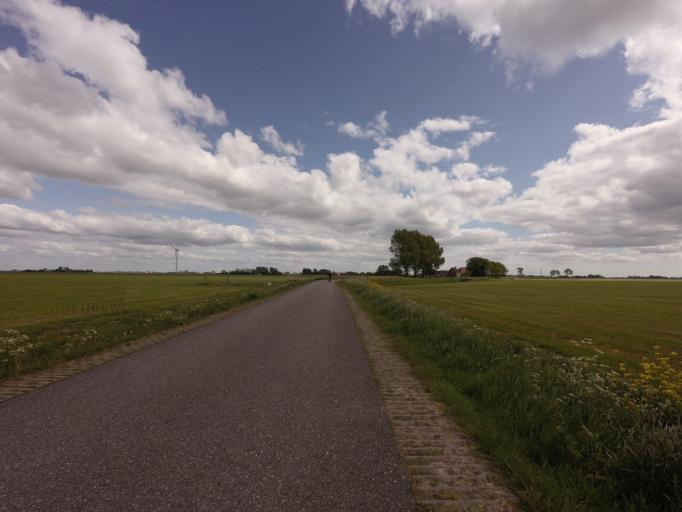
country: NL
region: Friesland
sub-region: Sudwest Fryslan
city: Bolsward
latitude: 53.0819
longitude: 5.5502
